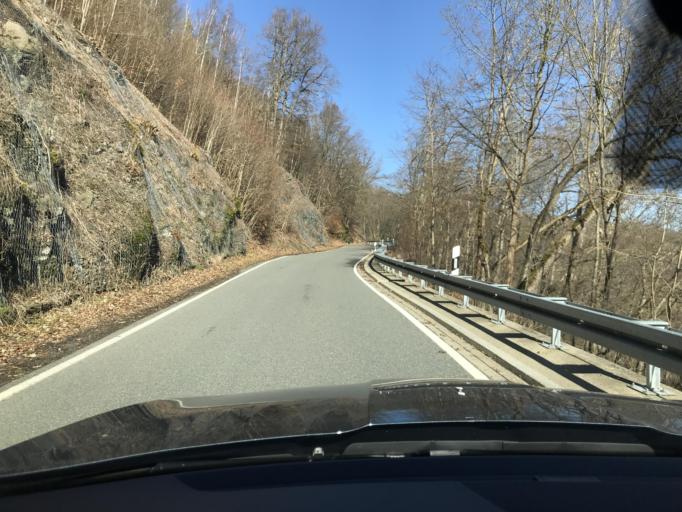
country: DE
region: Saxony-Anhalt
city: Timmenrode
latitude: 51.7255
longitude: 10.9674
